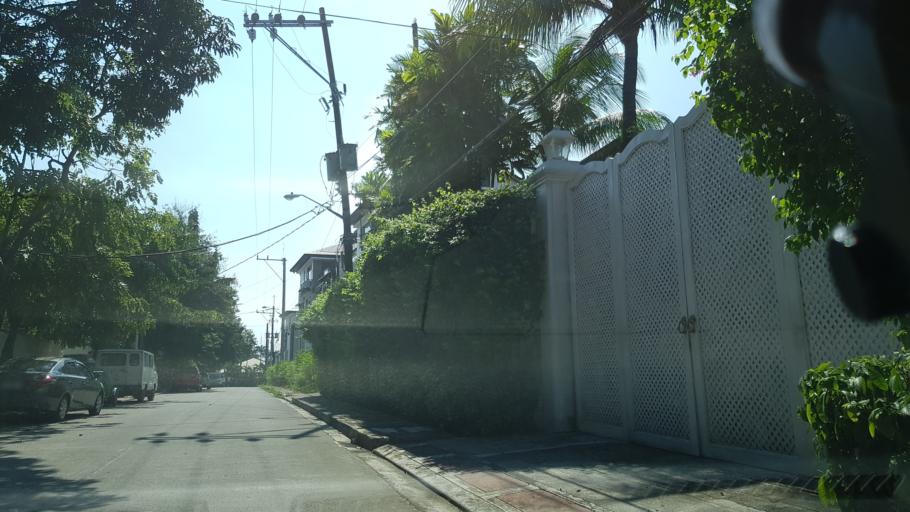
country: PH
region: Metro Manila
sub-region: San Juan
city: San Juan
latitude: 14.6144
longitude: 121.0299
